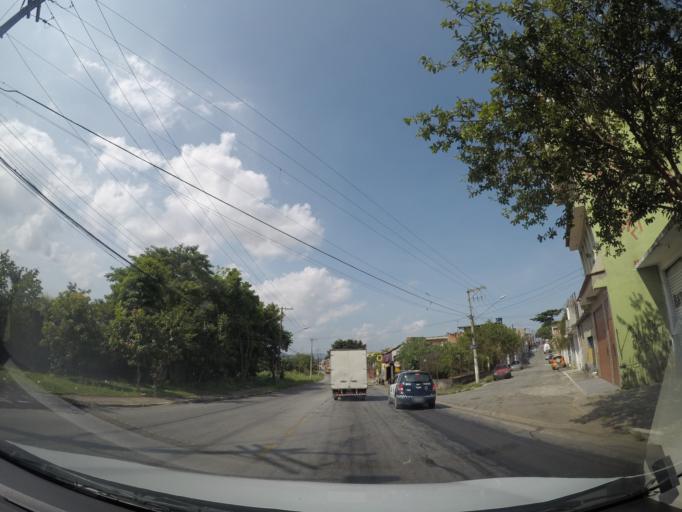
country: BR
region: Sao Paulo
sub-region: Guarulhos
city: Guarulhos
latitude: -23.4440
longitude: -46.4701
